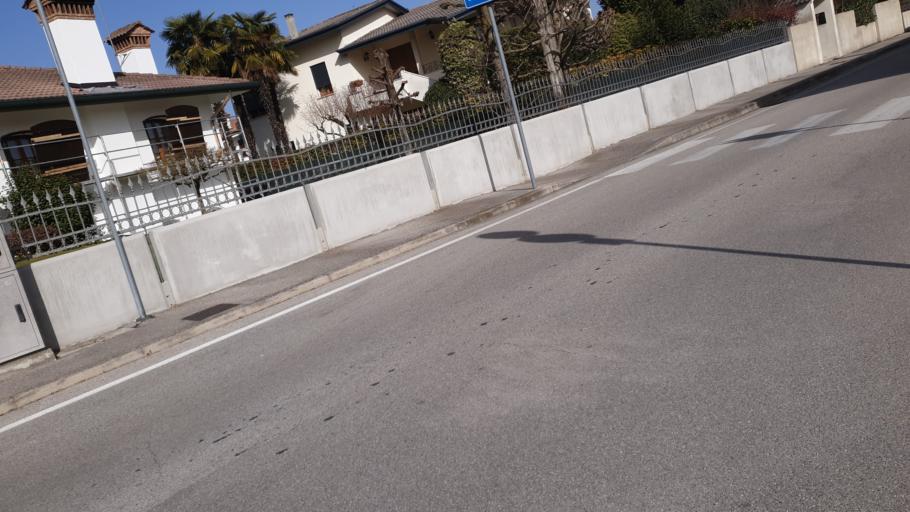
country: IT
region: Veneto
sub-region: Provincia di Padova
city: Mejaniga
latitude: 45.4643
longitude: 11.9111
